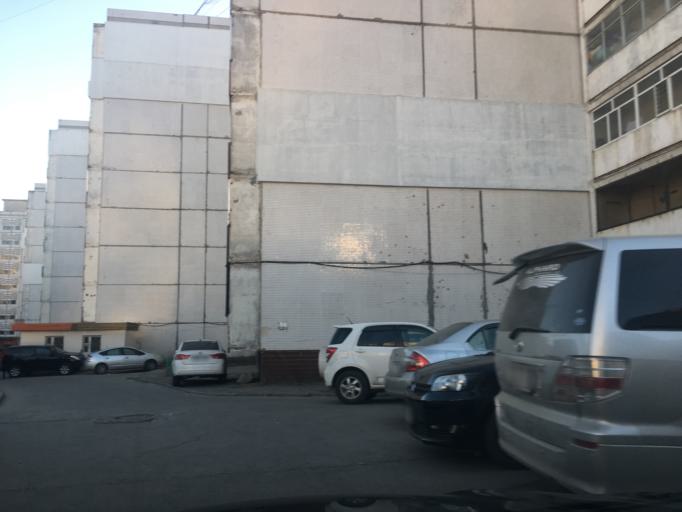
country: MN
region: Ulaanbaatar
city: Ulaanbaatar
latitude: 47.9199
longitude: 106.8811
